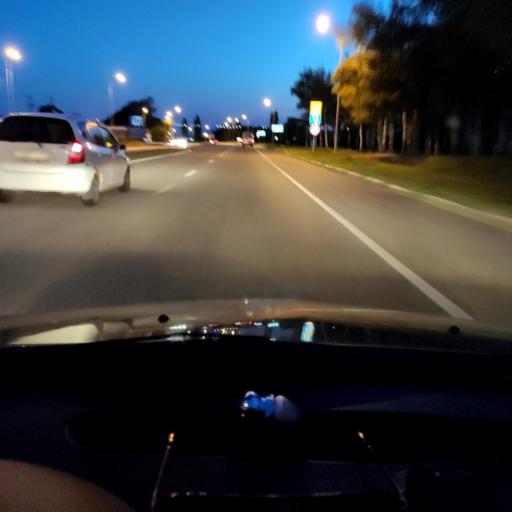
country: RU
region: Belgorod
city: Razumnoye
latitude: 50.6786
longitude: 36.7317
